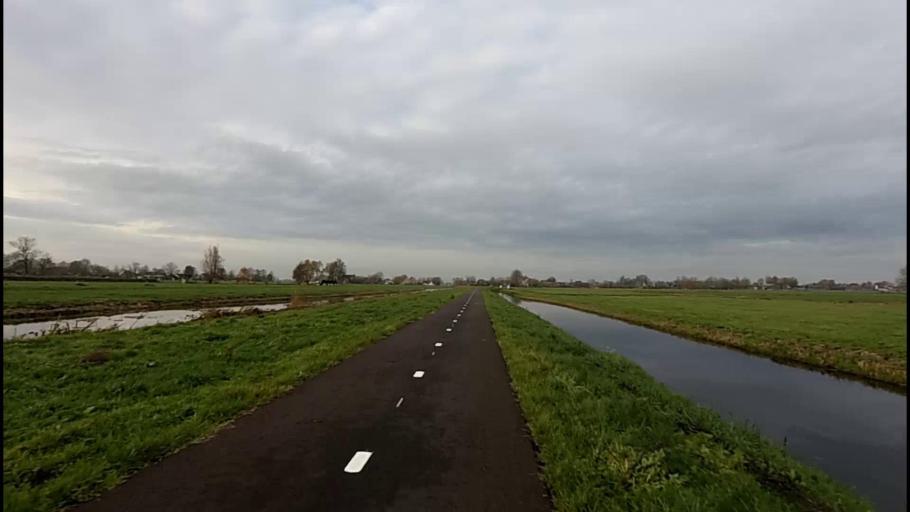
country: NL
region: South Holland
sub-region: Gemeente Vlist
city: Haastrecht
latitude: 51.9570
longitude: 4.7438
